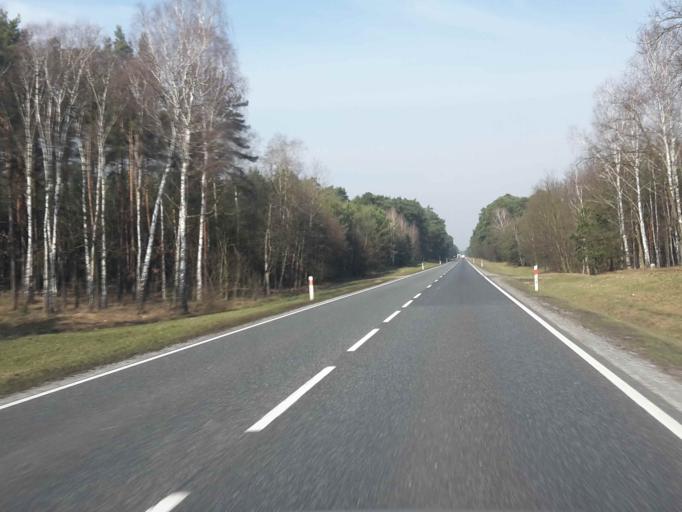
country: PL
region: Kujawsko-Pomorskie
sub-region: Powiat torunski
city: Wielka Nieszawka
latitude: 53.0045
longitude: 18.4465
